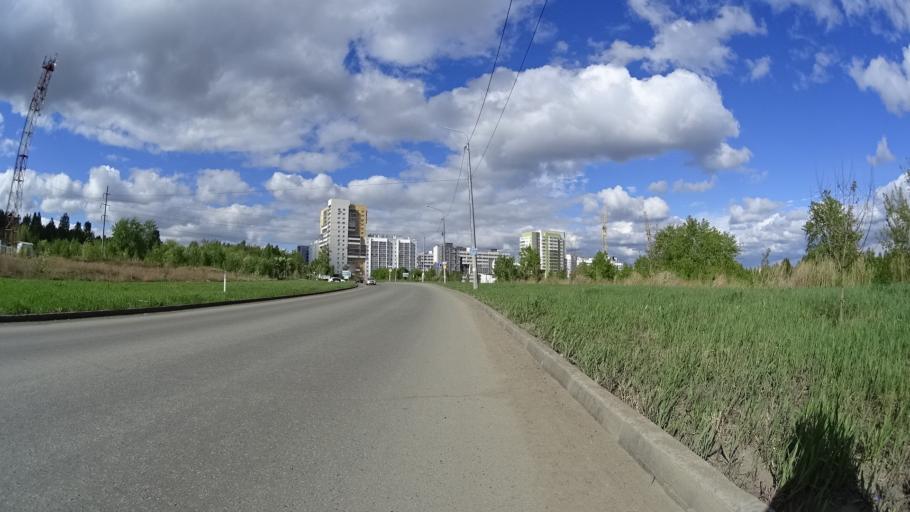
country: RU
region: Chelyabinsk
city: Sargazy
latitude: 55.1576
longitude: 61.2848
